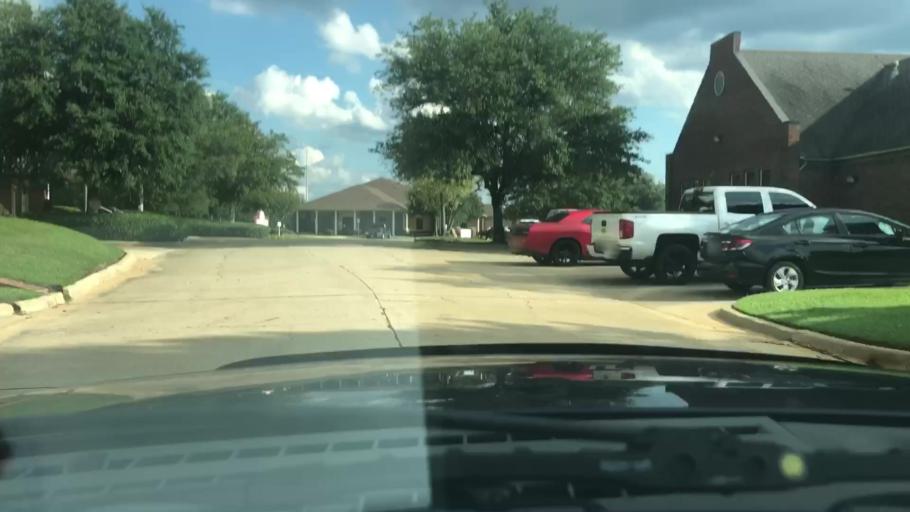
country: US
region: Arkansas
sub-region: Miller County
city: Texarkana
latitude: 33.4707
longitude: -94.0652
